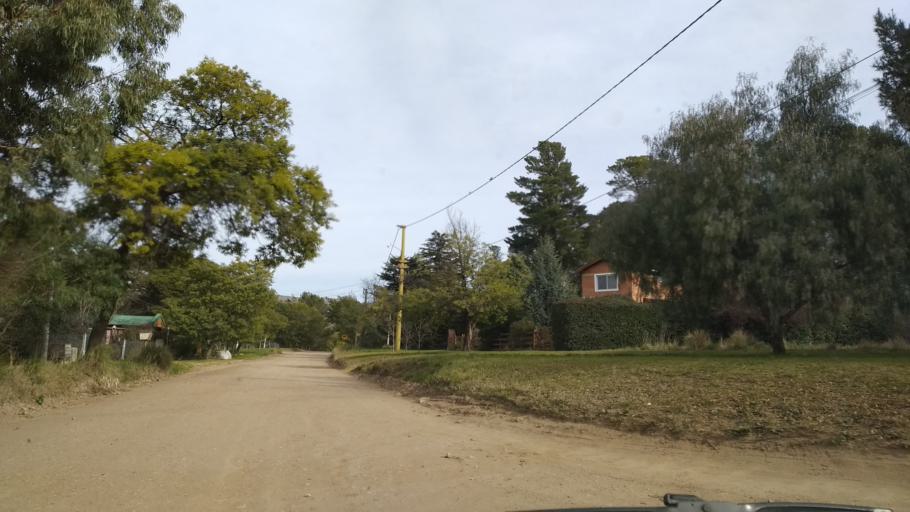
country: AR
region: Buenos Aires
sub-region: Partido de Tornquist
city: Tornquist
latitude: -38.0837
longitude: -61.9288
